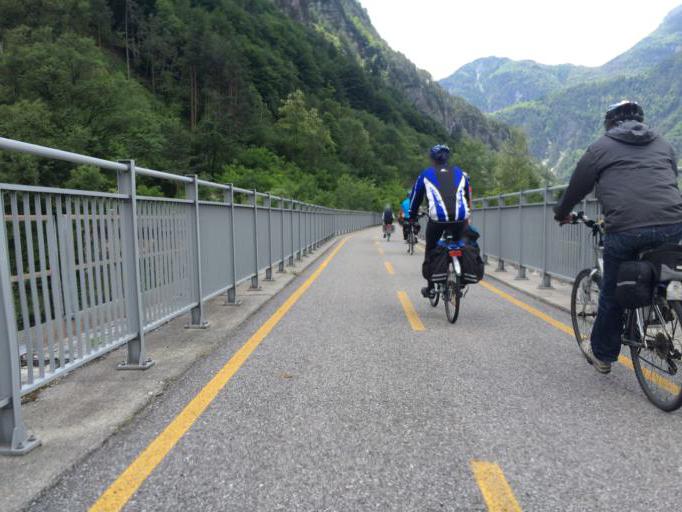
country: IT
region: Friuli Venezia Giulia
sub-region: Provincia di Udine
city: Dogna
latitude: 46.4479
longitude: 13.3181
